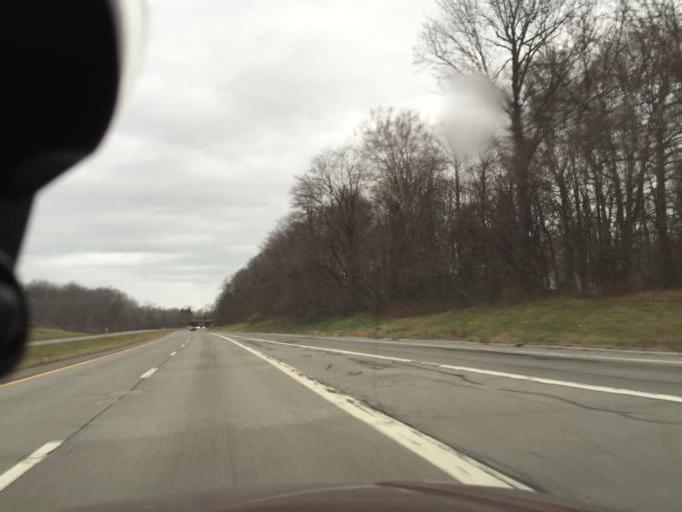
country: US
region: New York
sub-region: Monroe County
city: Greece
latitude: 43.2333
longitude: -77.6717
